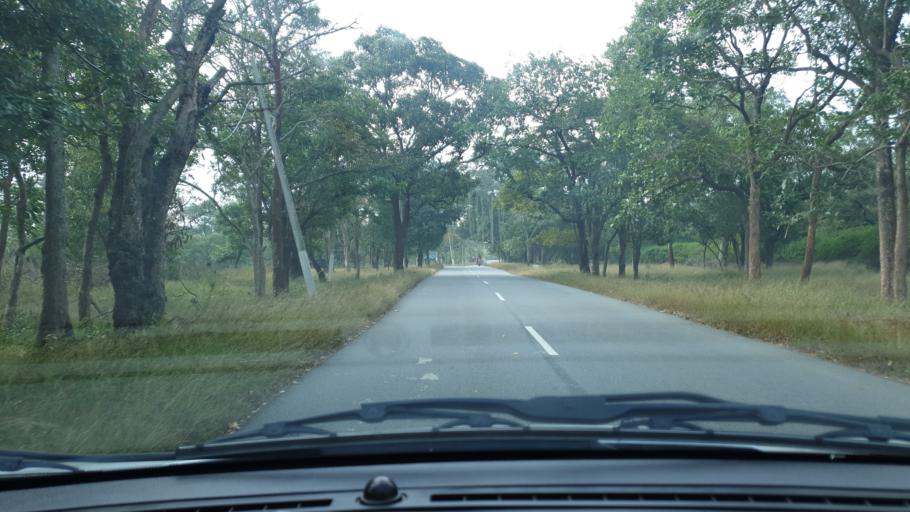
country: IN
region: Andhra Pradesh
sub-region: Kurnool
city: Srisailam
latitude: 16.2832
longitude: 78.7268
